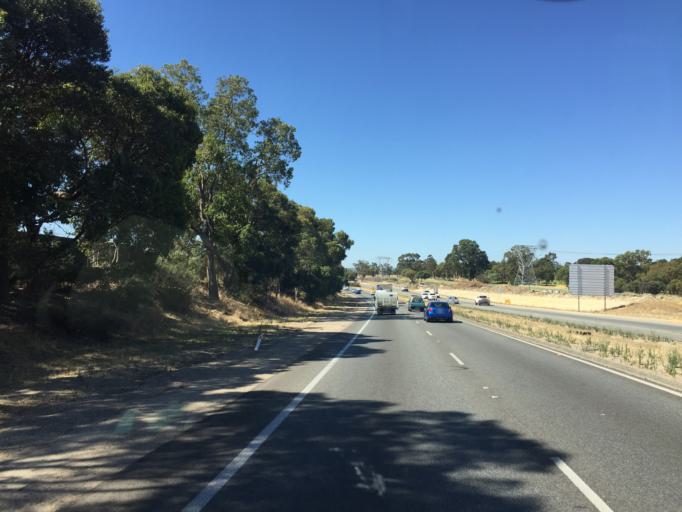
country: AU
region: Western Australia
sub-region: Kalamunda
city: Maida Vale
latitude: -31.9390
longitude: 116.0168
